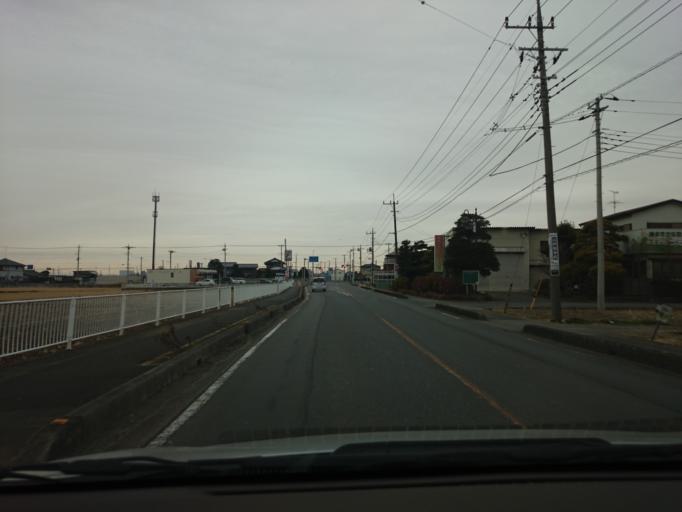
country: JP
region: Saitama
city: Kisai
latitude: 36.1084
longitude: 139.5912
